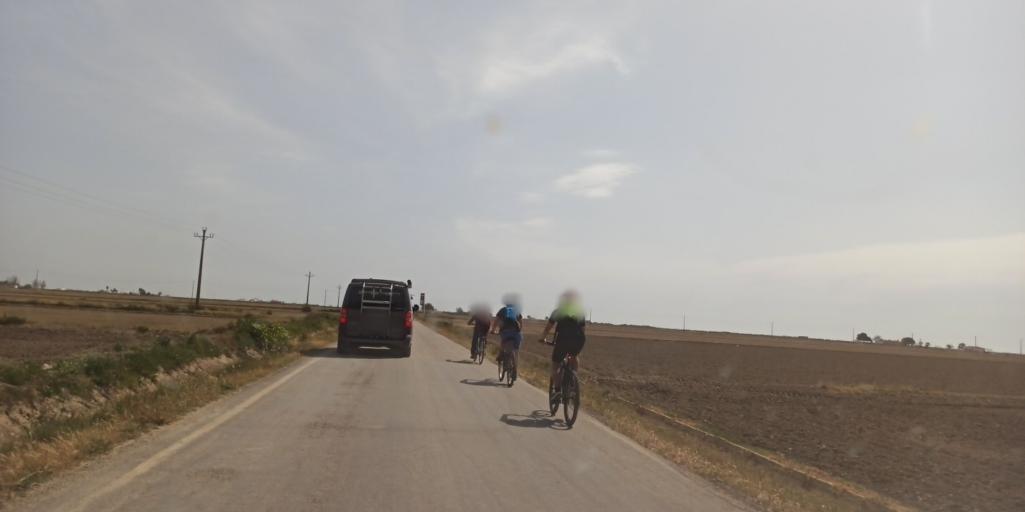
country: ES
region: Catalonia
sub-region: Provincia de Tarragona
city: Deltebre
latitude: 40.6459
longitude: 0.7192
